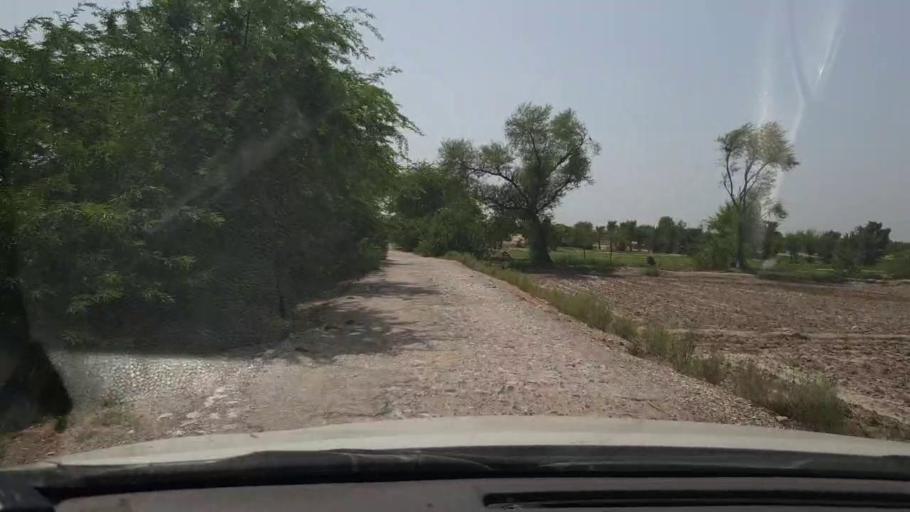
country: PK
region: Sindh
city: Rohri
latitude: 27.5213
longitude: 69.0929
